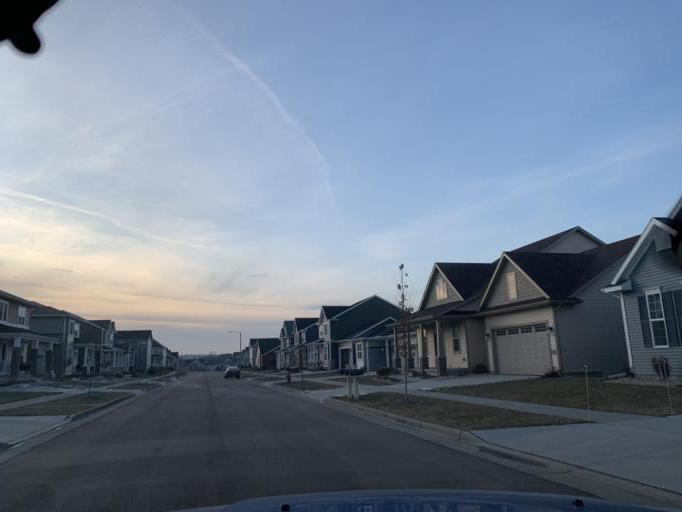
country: US
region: Wisconsin
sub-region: Dane County
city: Verona
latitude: 43.0502
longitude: -89.5535
